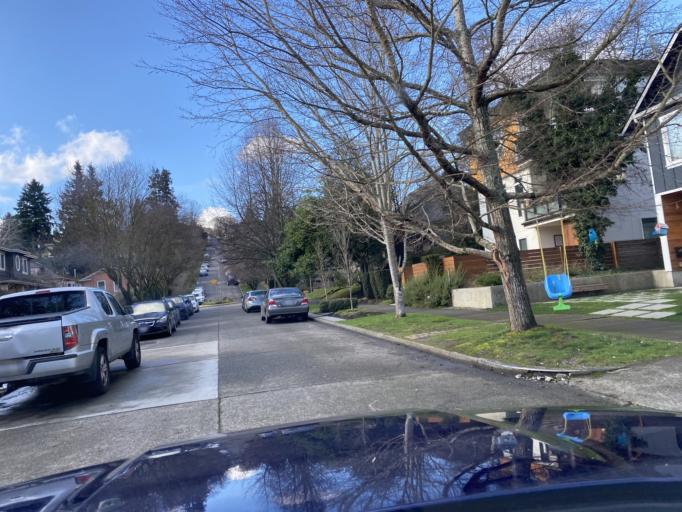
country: US
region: Washington
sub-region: King County
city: Seattle
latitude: 47.6259
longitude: -122.2955
